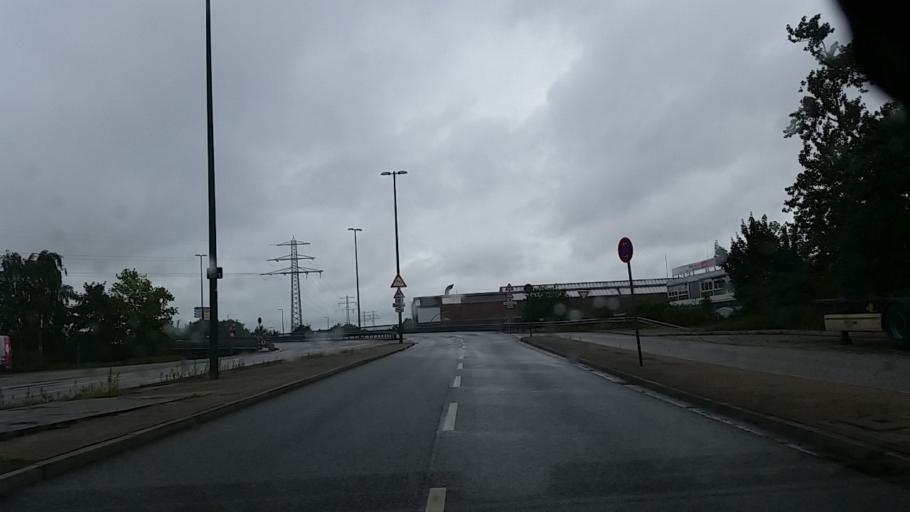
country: DE
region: Hamburg
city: Kleiner Grasbrook
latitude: 53.5157
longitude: 9.9697
